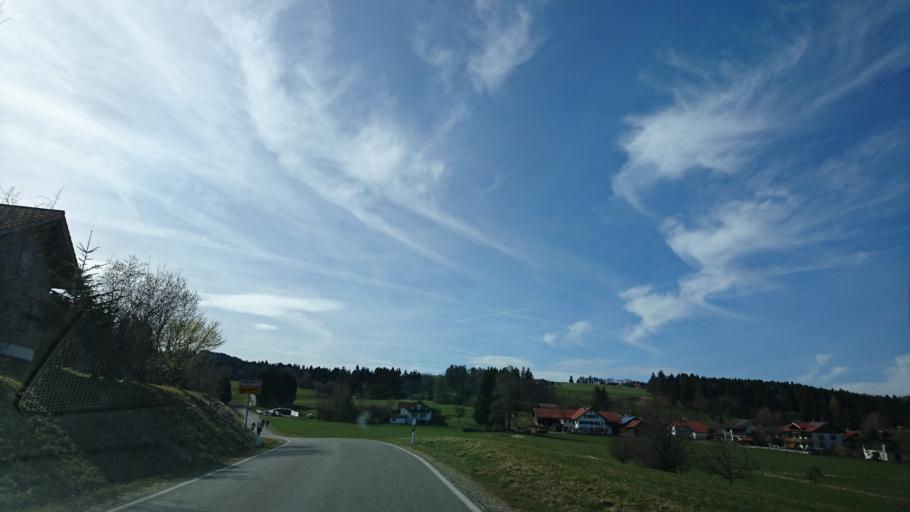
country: DE
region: Bavaria
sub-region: Upper Bavaria
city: Bernbeuren
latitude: 47.7371
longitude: 10.7729
